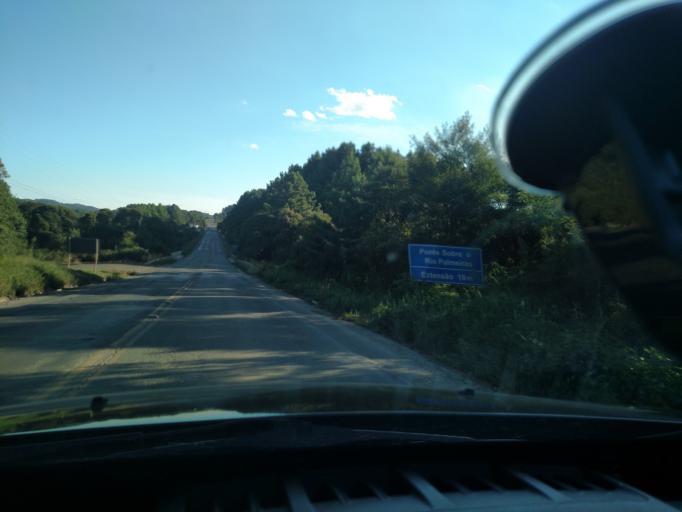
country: BR
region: Santa Catarina
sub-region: Otacilio Costa
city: Otacilio Costa
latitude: -27.5850
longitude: -50.1654
